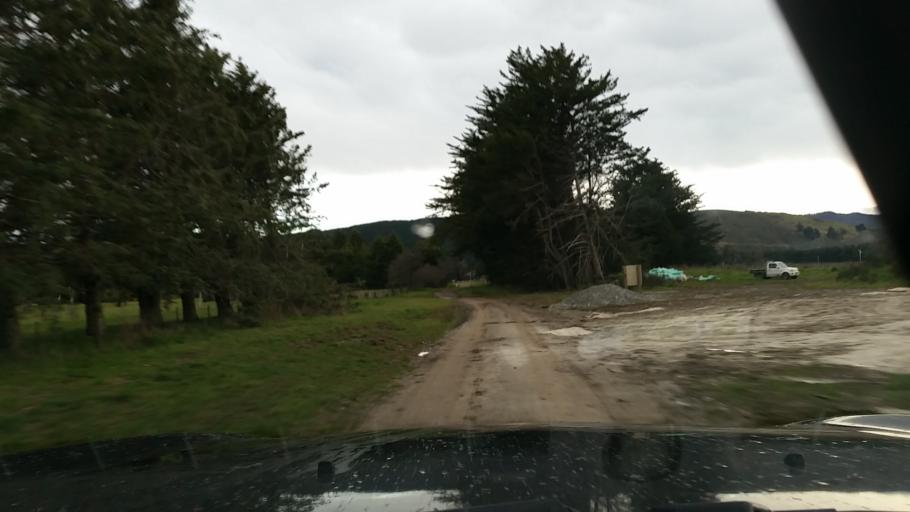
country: NZ
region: Nelson
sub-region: Nelson City
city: Nelson
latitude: -41.5607
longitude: 173.5213
